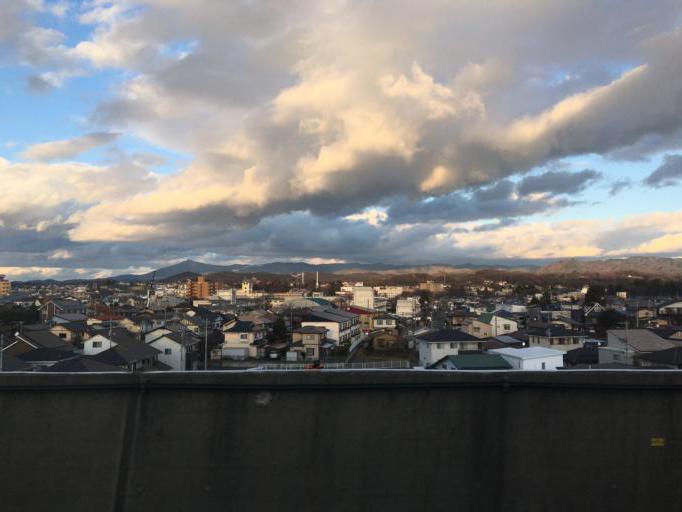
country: JP
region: Iwate
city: Morioka-shi
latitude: 39.7111
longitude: 141.1258
